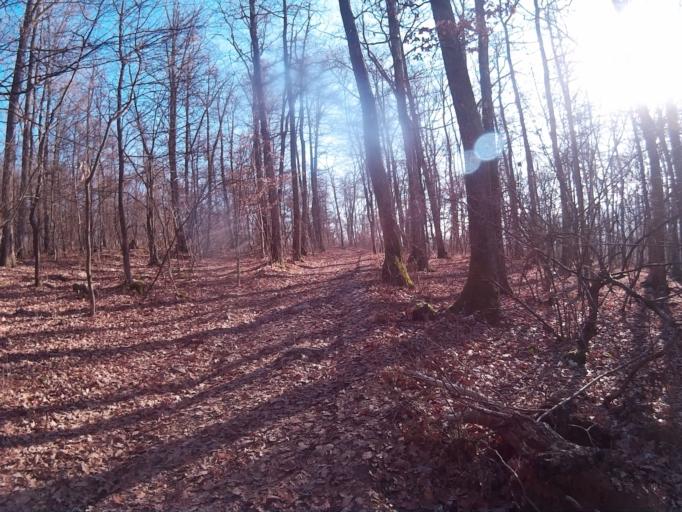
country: HU
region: Borsod-Abauj-Zemplen
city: Rudabanya
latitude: 48.4888
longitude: 20.5771
